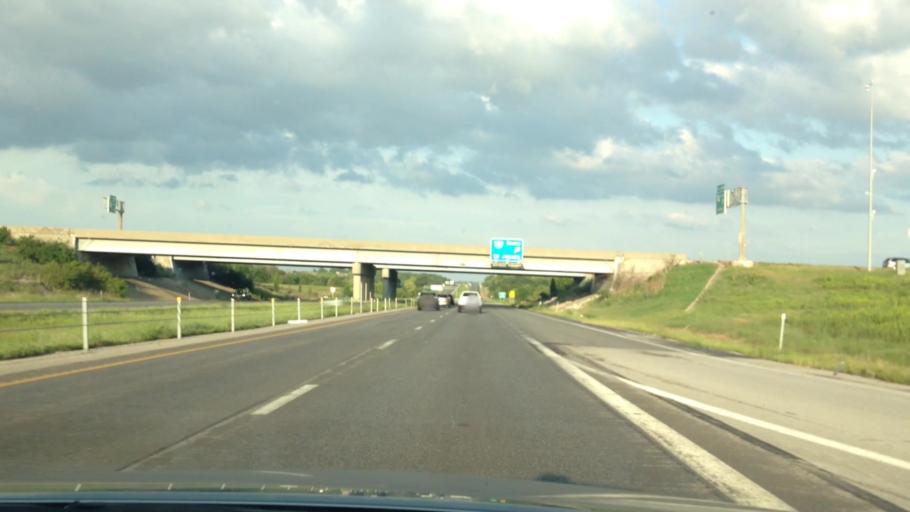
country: US
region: Missouri
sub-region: Clay County
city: Pleasant Valley
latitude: 39.2431
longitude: -94.5092
